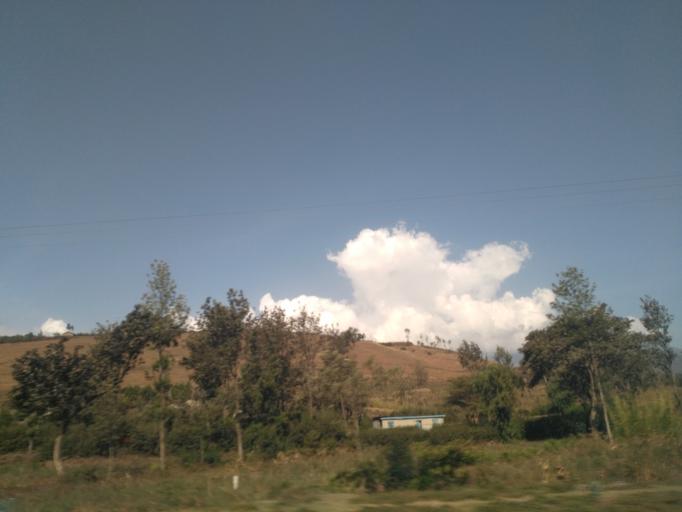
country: TZ
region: Arusha
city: Arusha
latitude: -3.2237
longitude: 36.6063
